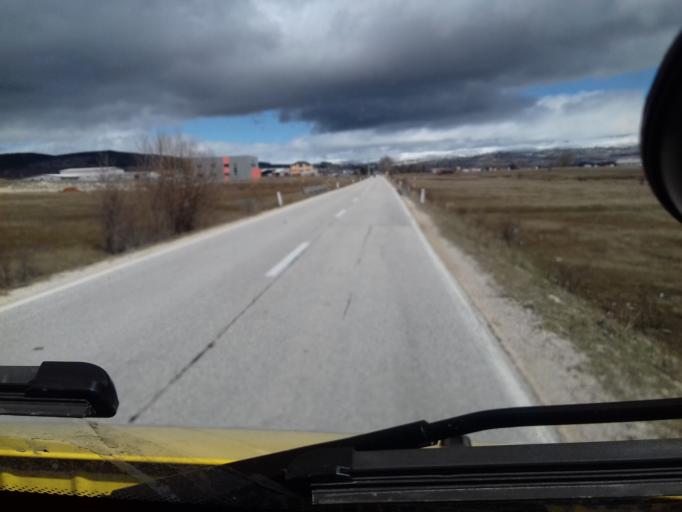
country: BA
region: Federation of Bosnia and Herzegovina
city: Tomislavgrad
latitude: 43.6770
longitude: 17.1998
